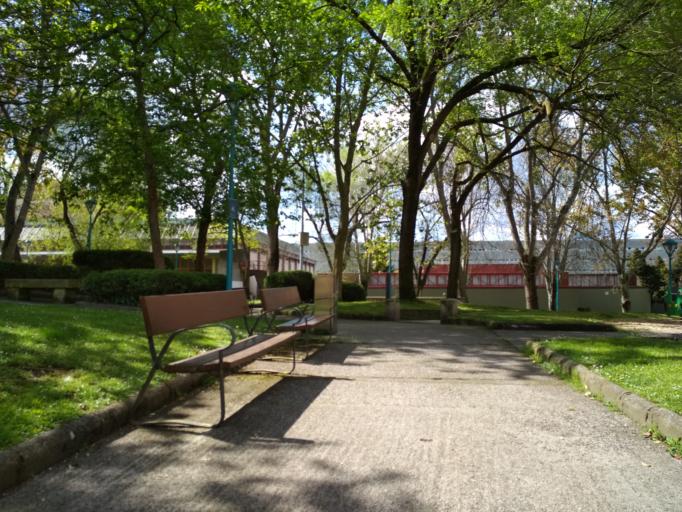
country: ES
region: Galicia
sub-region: Provincia da Coruna
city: A Coruna
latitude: 43.3453
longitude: -8.4020
